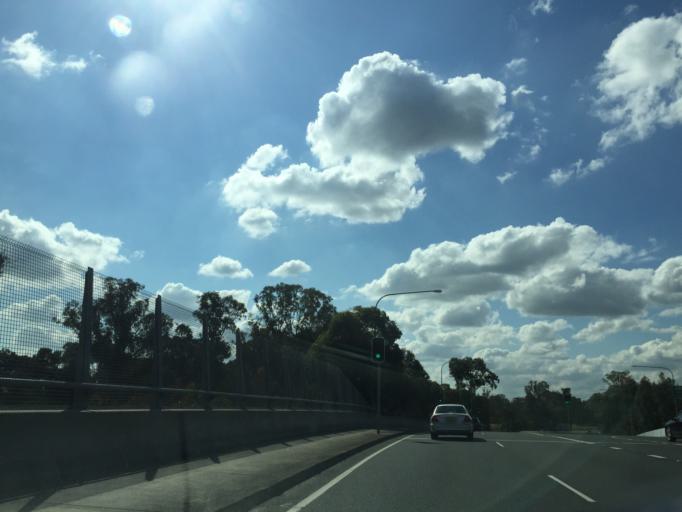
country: AU
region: New South Wales
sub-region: Blacktown
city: Quakers Hill
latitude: -33.7336
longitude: 150.8744
